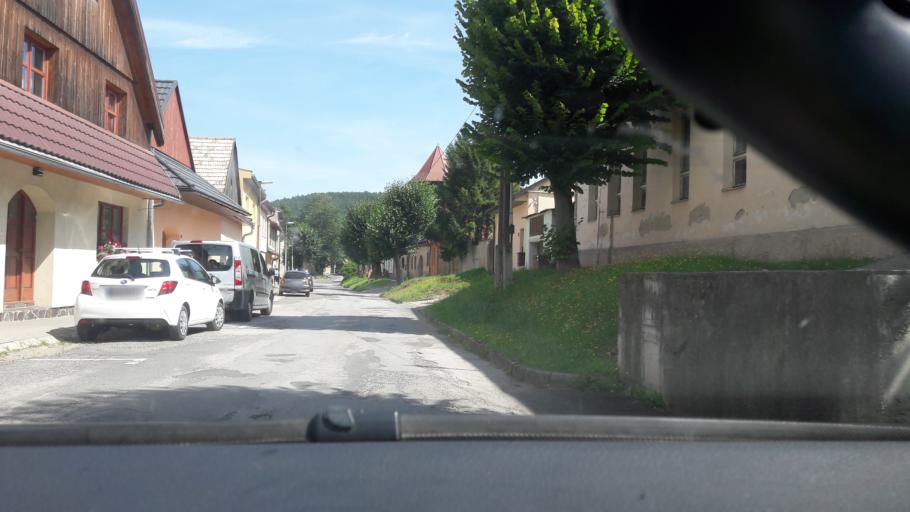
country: SK
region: Presovsky
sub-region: Okres Presov
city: Kezmarok
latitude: 49.1385
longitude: 20.4311
